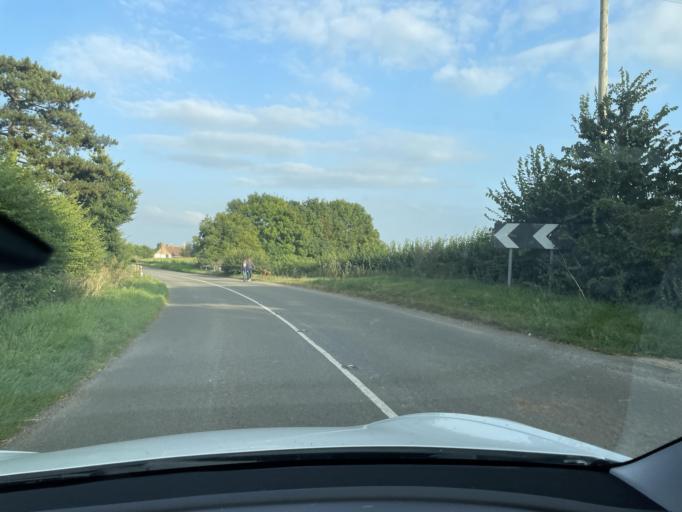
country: GB
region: England
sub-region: Northamptonshire
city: Raunds
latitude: 52.3703
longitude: -0.4530
